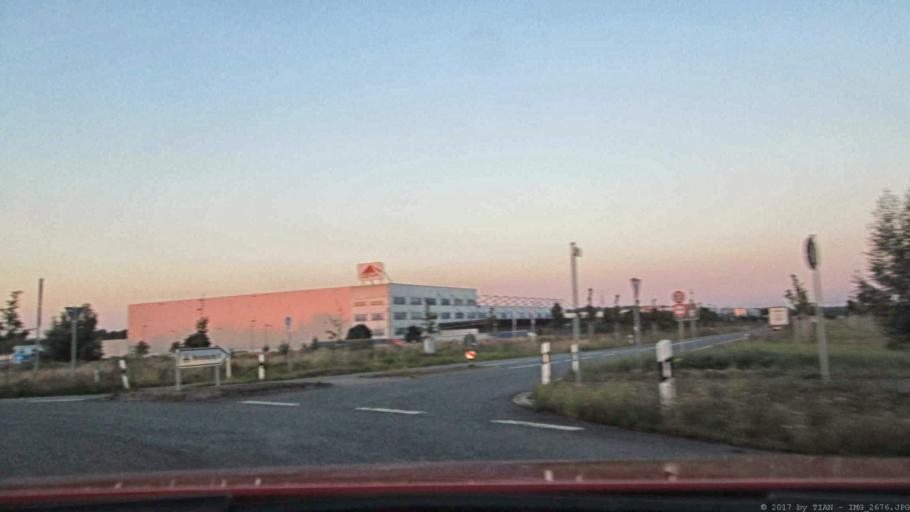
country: DE
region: Lower Saxony
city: Wolfsburg
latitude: 52.3693
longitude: 10.7461
